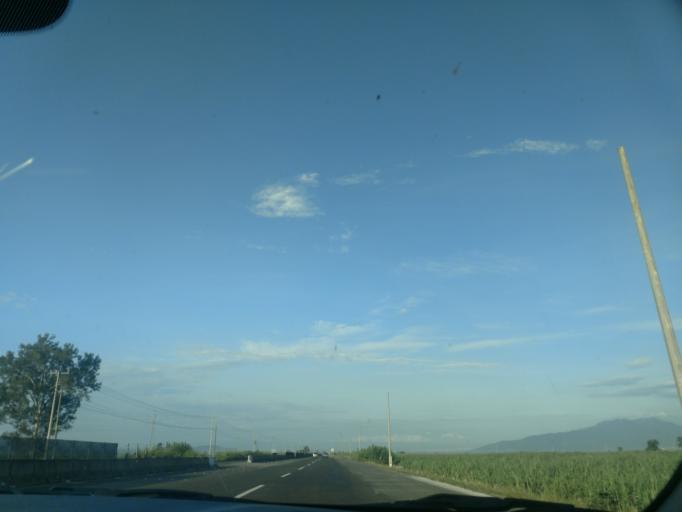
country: MX
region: Jalisco
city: El Refugio
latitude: 20.6439
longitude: -103.7551
